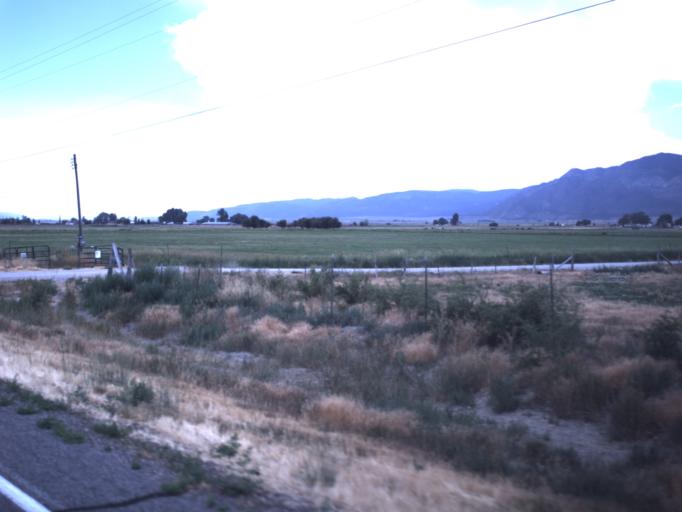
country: US
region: Utah
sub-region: Sanpete County
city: Moroni
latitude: 39.4871
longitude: -111.5631
